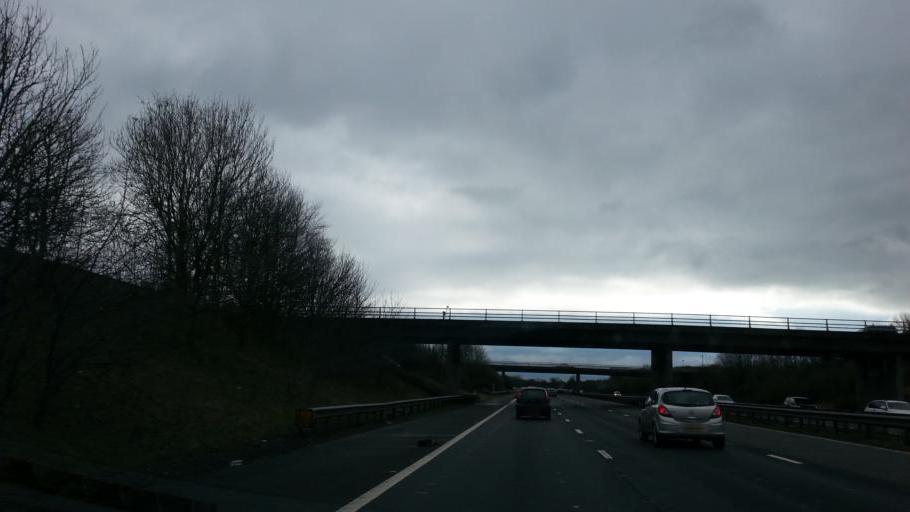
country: GB
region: England
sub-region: Somerset
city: North Petherton
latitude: 51.1028
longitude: -2.9927
